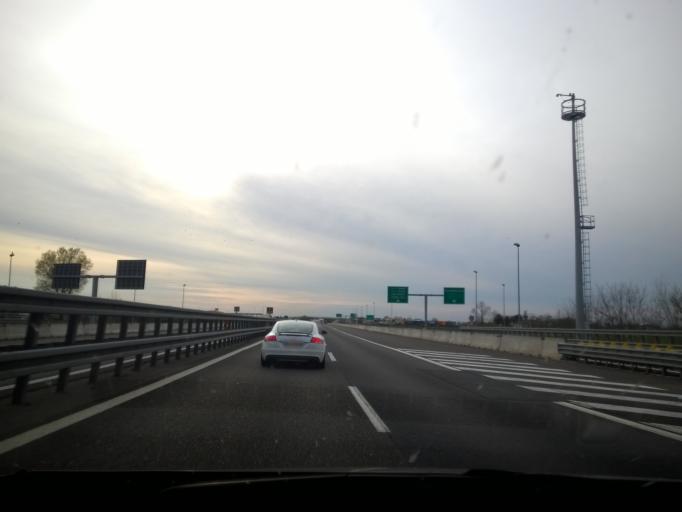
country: IT
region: Lombardy
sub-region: Provincia di Lodi
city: San Rocco al Porto
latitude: 45.0612
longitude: 9.6577
